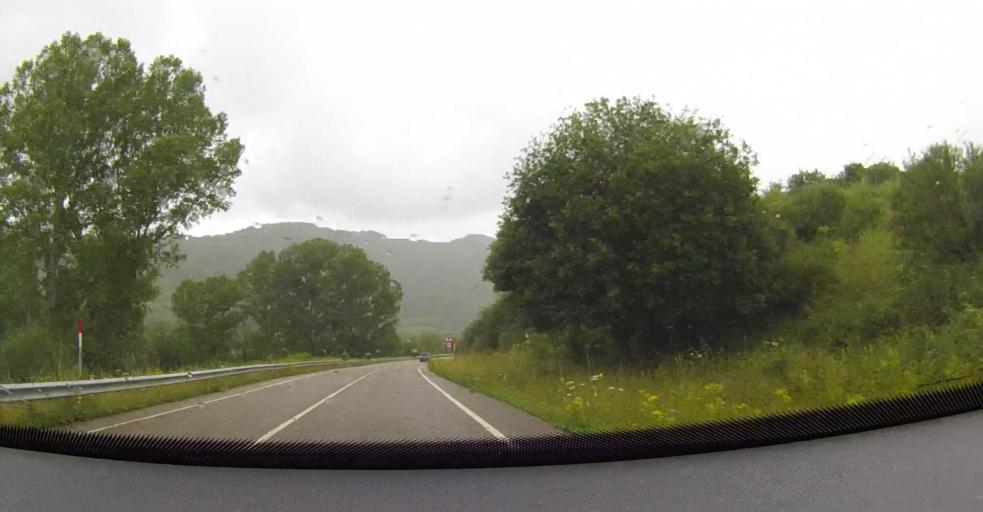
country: ES
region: Castille and Leon
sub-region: Provincia de Leon
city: Acebedo
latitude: 43.0445
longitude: -5.1184
